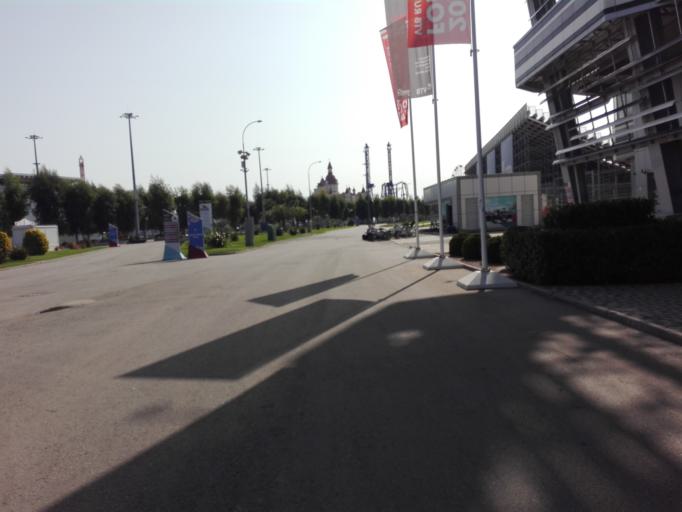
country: RU
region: Krasnodarskiy
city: Adler
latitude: 43.4086
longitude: 39.9682
